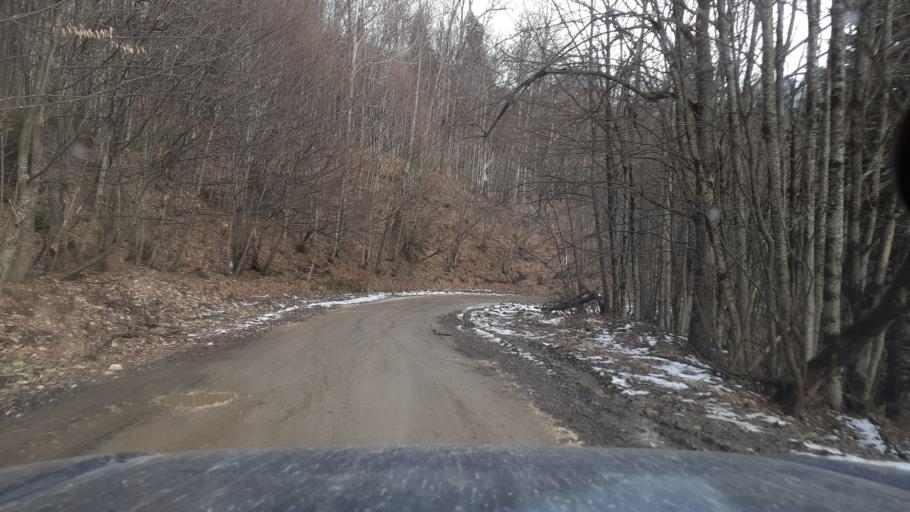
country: RU
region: Krasnodarskiy
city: Neftegorsk
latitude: 44.0739
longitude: 39.7806
